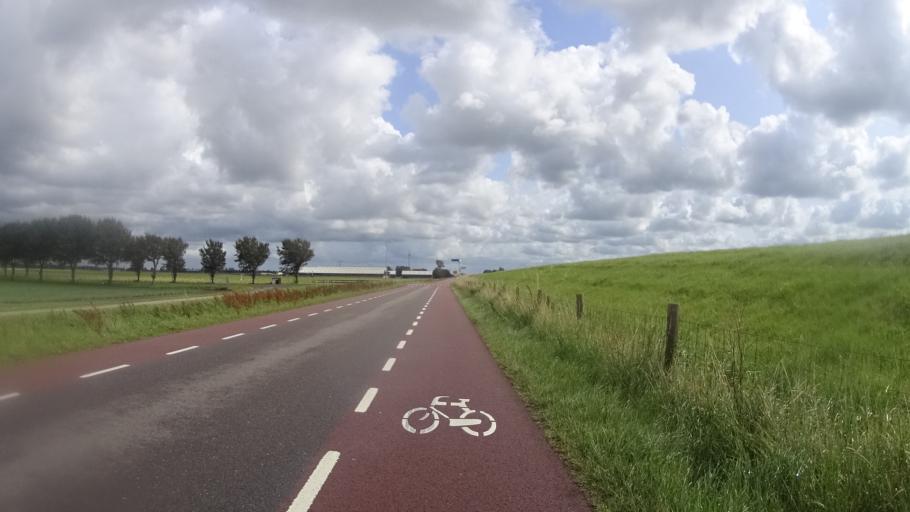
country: NL
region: North Holland
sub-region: Gemeente Schagen
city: Schagen
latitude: 52.8254
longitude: 4.8190
